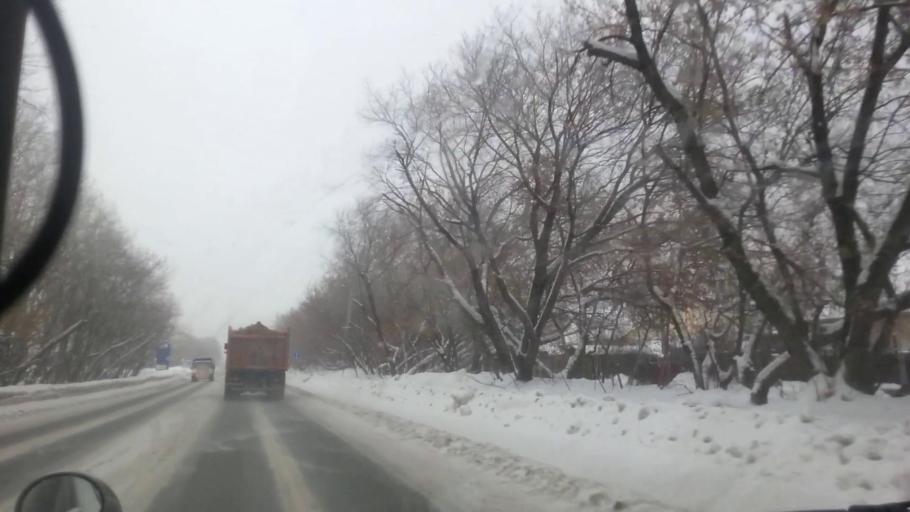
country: RU
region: Altai Krai
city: Vlasikha
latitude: 53.3010
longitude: 83.5977
